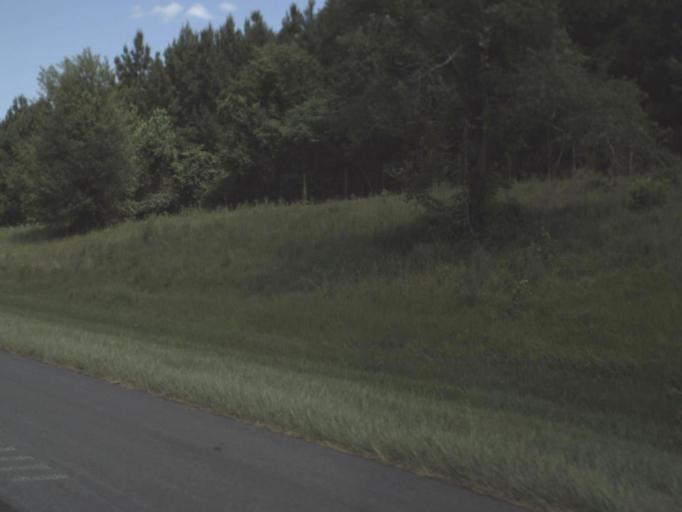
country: US
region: Florida
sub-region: Madison County
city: Madison
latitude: 30.4354
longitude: -83.4694
